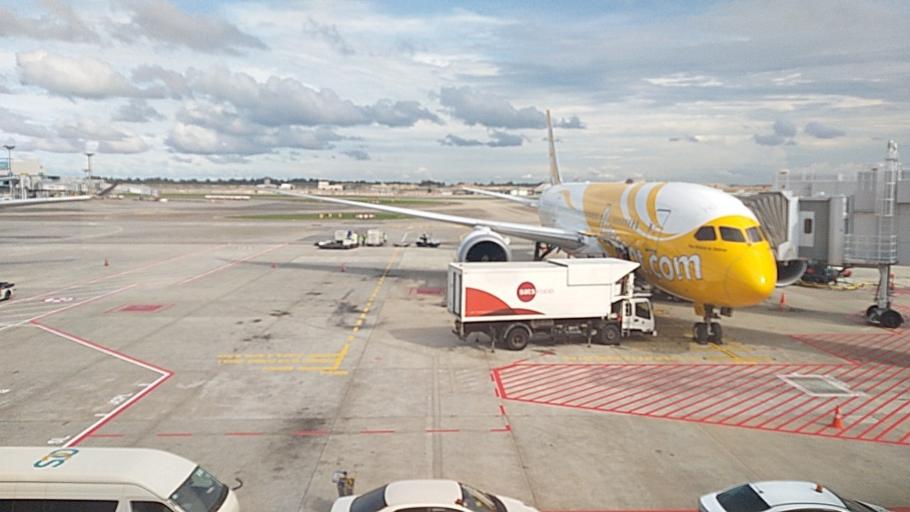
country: SG
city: Singapore
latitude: 1.3609
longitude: 103.9881
